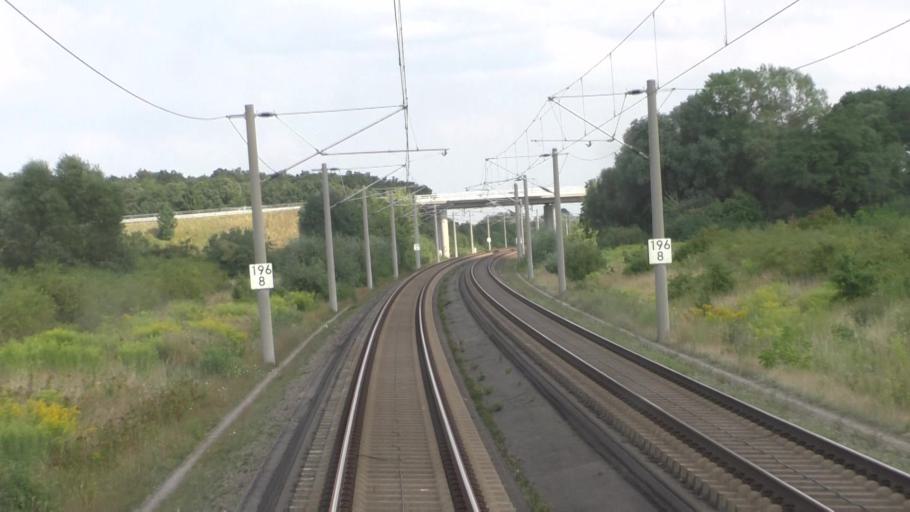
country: DE
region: Saxony-Anhalt
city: Tangermunde
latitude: 52.6008
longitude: 11.9747
